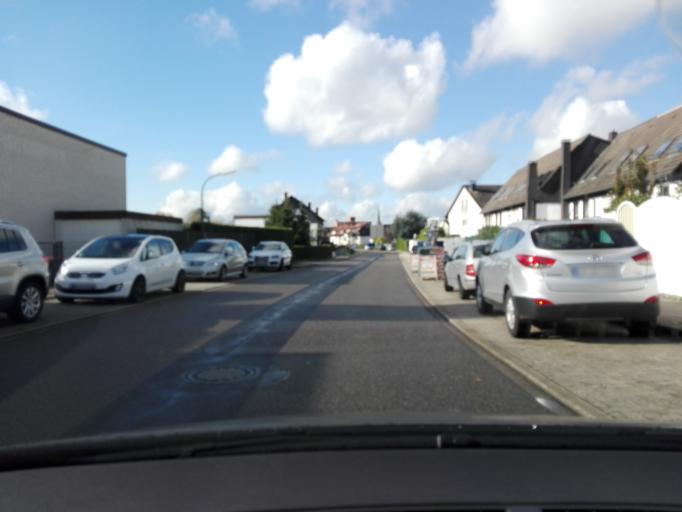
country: DE
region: North Rhine-Westphalia
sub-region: Regierungsbezirk Arnsberg
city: Holzwickede
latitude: 51.5000
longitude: 7.6286
